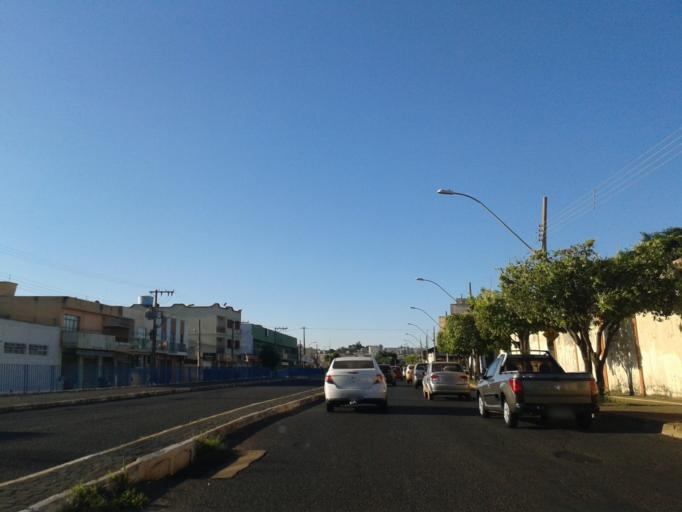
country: BR
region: Minas Gerais
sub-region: Uberlandia
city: Uberlandia
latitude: -18.9028
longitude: -48.2718
